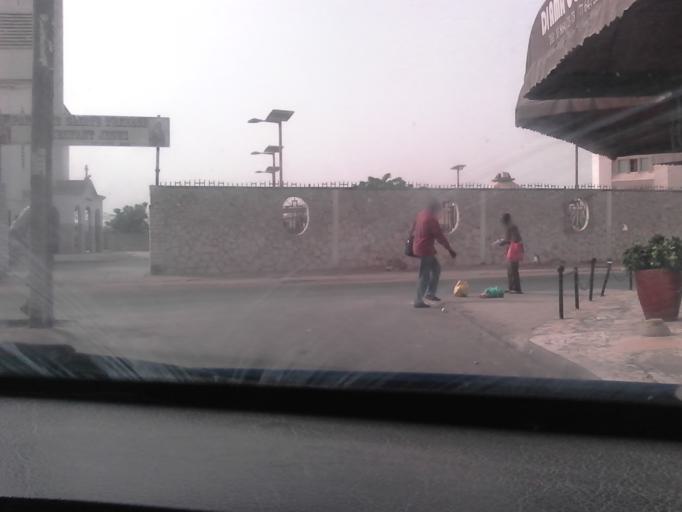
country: SN
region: Dakar
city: Dakar
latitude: 14.7009
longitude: -17.4535
